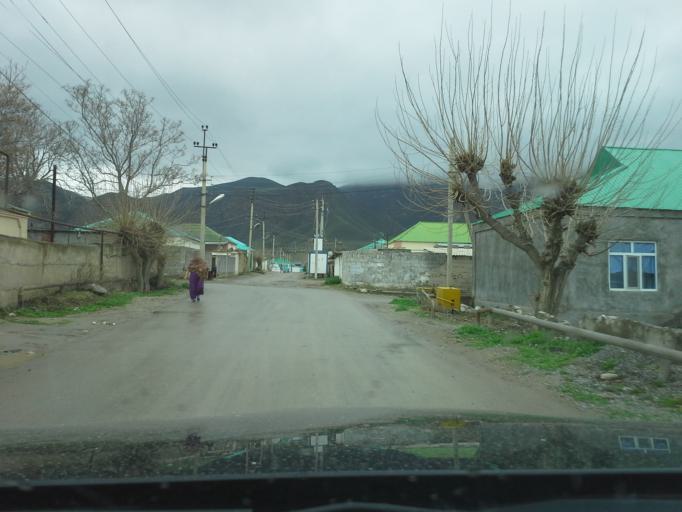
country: TM
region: Ahal
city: Abadan
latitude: 37.9550
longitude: 58.2065
